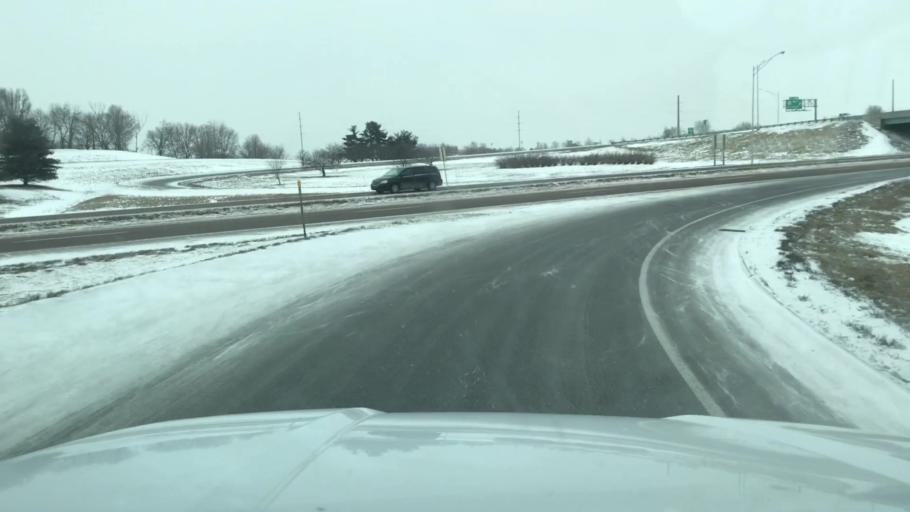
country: US
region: Missouri
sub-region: Buchanan County
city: Saint Joseph
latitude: 39.7485
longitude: -94.7910
